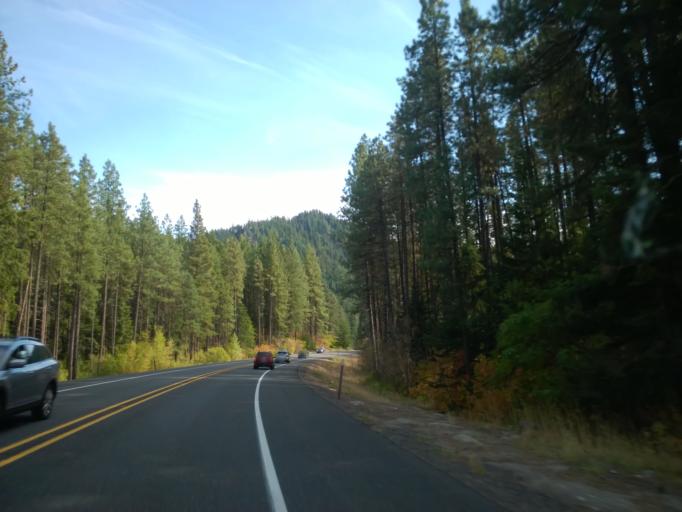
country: US
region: Washington
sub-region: Chelan County
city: Leavenworth
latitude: 47.7263
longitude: -120.7367
